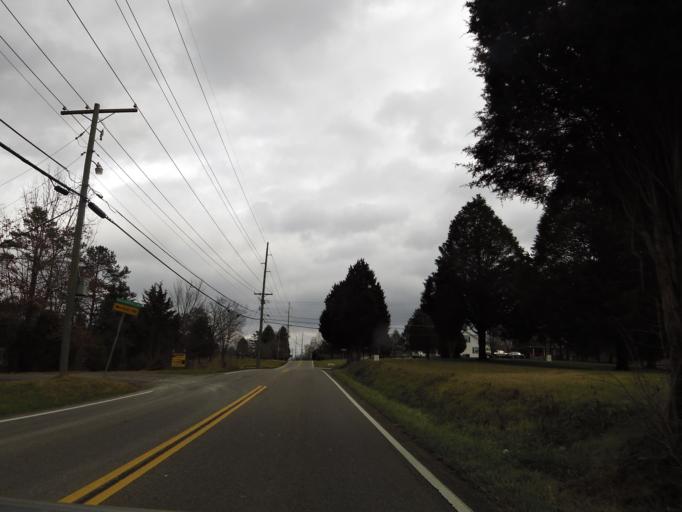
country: US
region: Tennessee
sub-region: Union County
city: Condon
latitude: 36.1035
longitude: -83.8940
